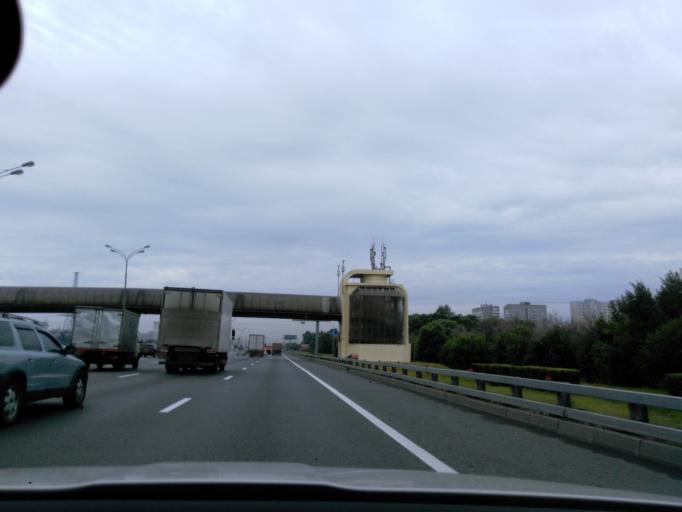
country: RU
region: Moscow
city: Ivanovskoye
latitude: 55.7631
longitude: 37.8426
